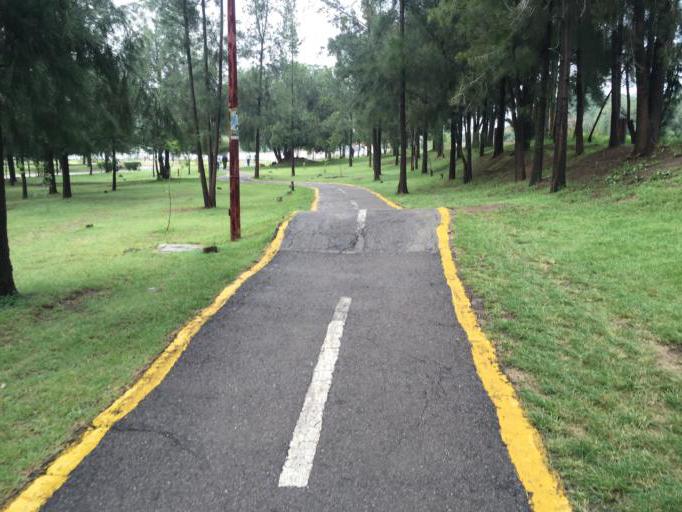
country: MX
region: Mexico
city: Cuautitlan Izcalli
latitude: 19.6505
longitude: -99.2247
